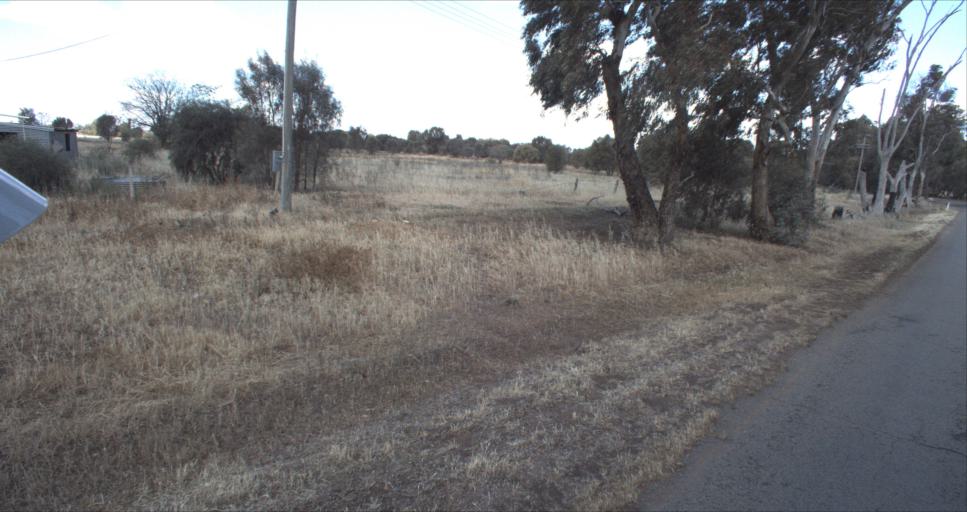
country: AU
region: New South Wales
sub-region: Leeton
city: Leeton
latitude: -34.5126
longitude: 146.2324
